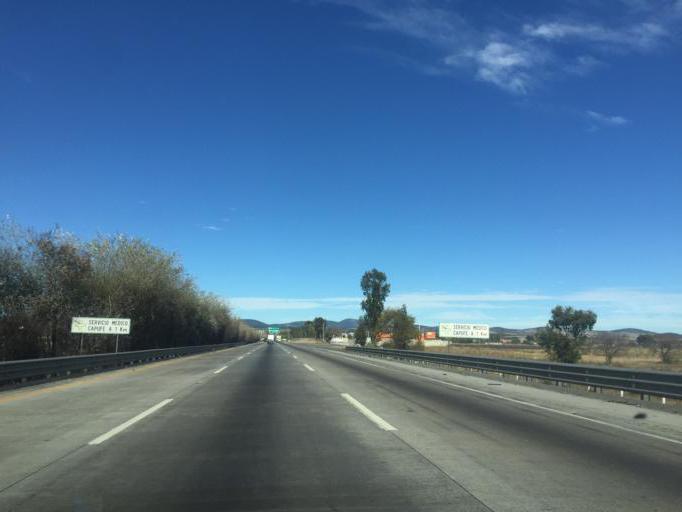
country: MX
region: Mexico
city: San Francisco Soyaniquilpan
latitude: 20.0107
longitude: -99.5098
